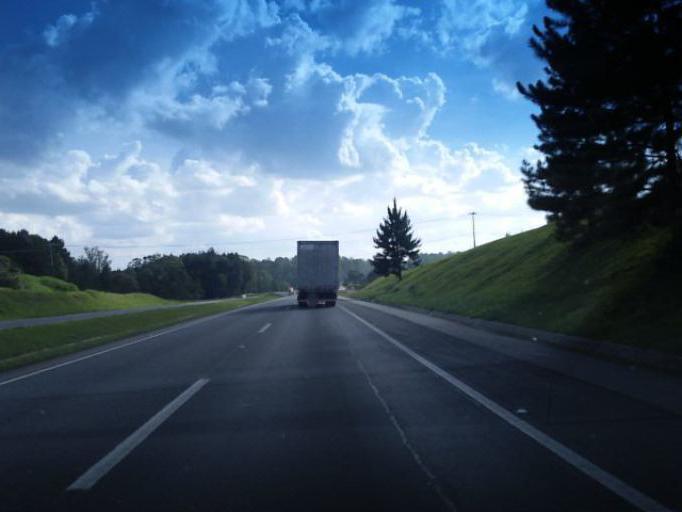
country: BR
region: Parana
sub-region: Piraquara
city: Piraquara
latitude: -25.4199
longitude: -49.0715
